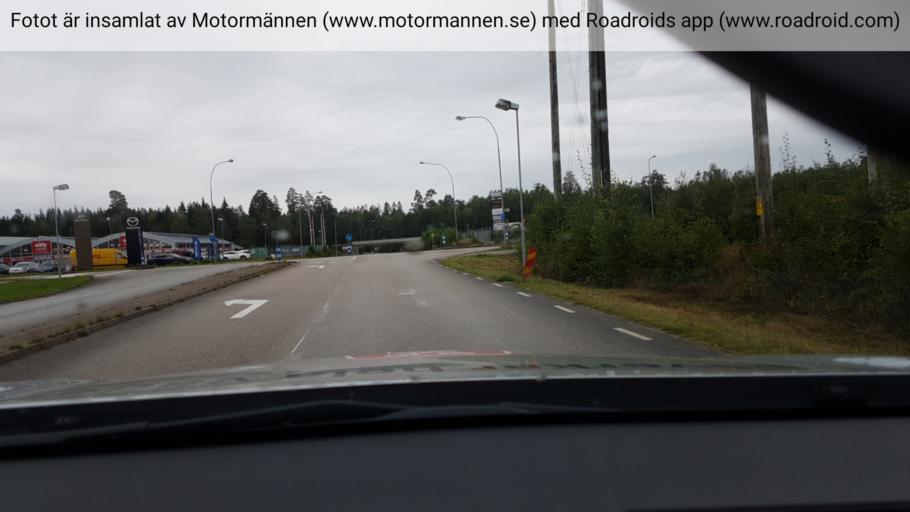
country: SE
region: Vaestra Goetaland
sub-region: Trollhattan
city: Trollhattan
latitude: 58.3403
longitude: 12.2541
